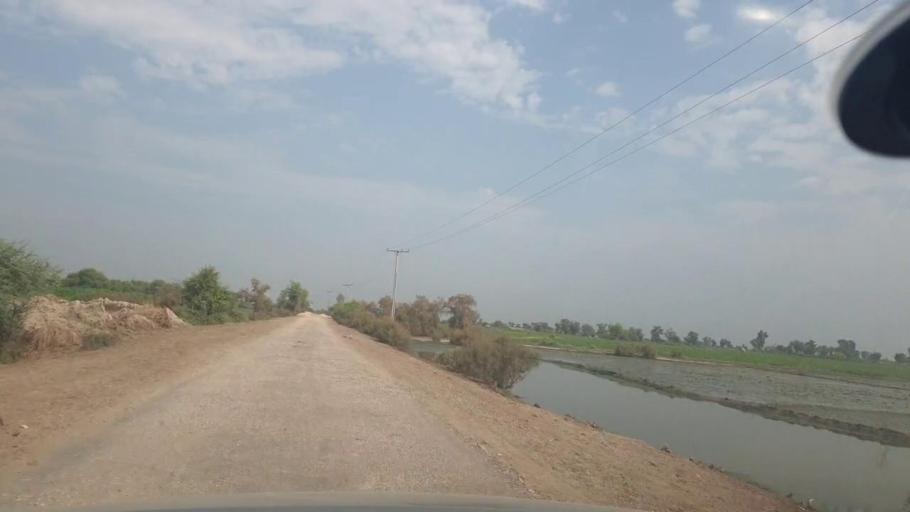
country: PK
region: Balochistan
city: Mehrabpur
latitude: 28.0648
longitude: 68.1038
